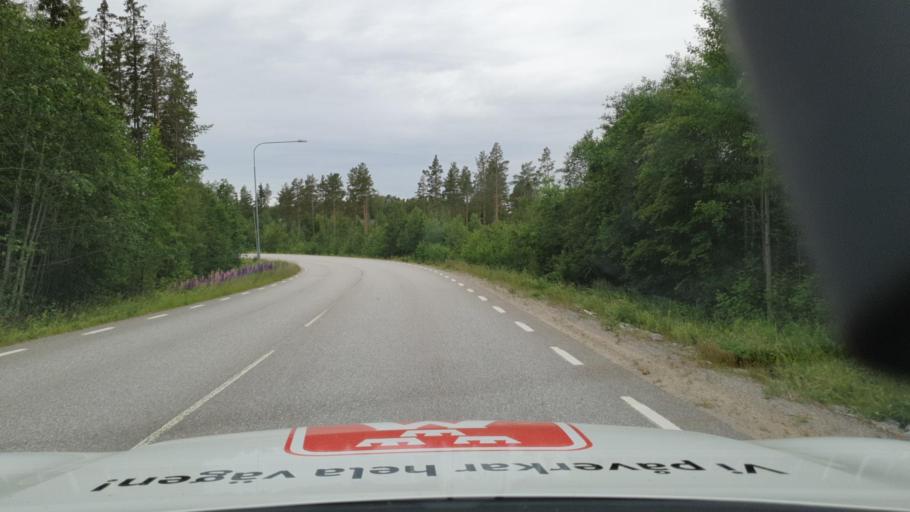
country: SE
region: Vaesterbotten
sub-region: Nordmalings Kommun
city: Nordmaling
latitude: 63.5340
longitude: 19.4047
